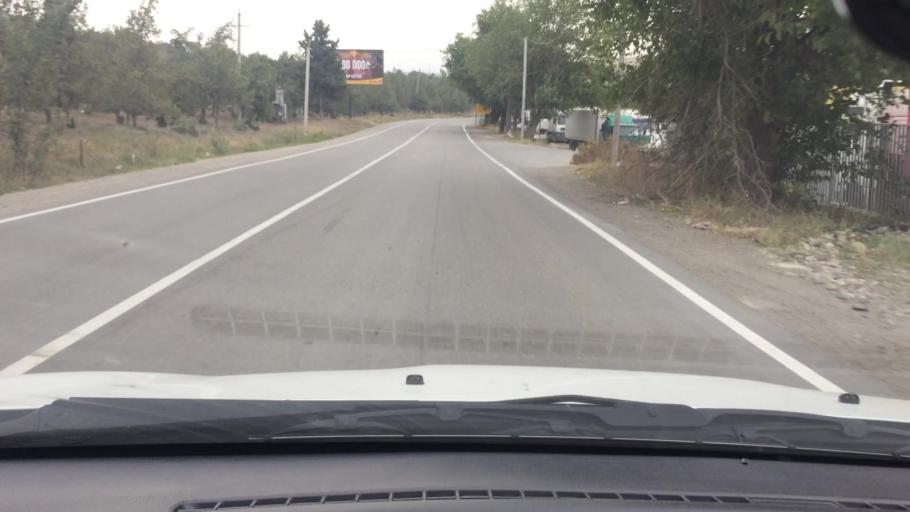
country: GE
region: Kvemo Kartli
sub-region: Gardabani
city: Gardabani
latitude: 41.3403
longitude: 45.0689
